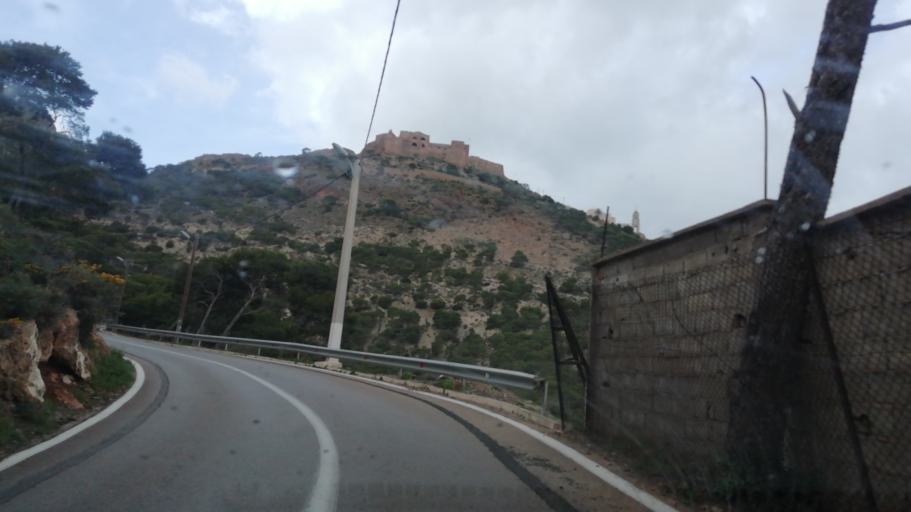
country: DZ
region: Oran
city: Oran
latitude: 35.7044
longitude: -0.6621
